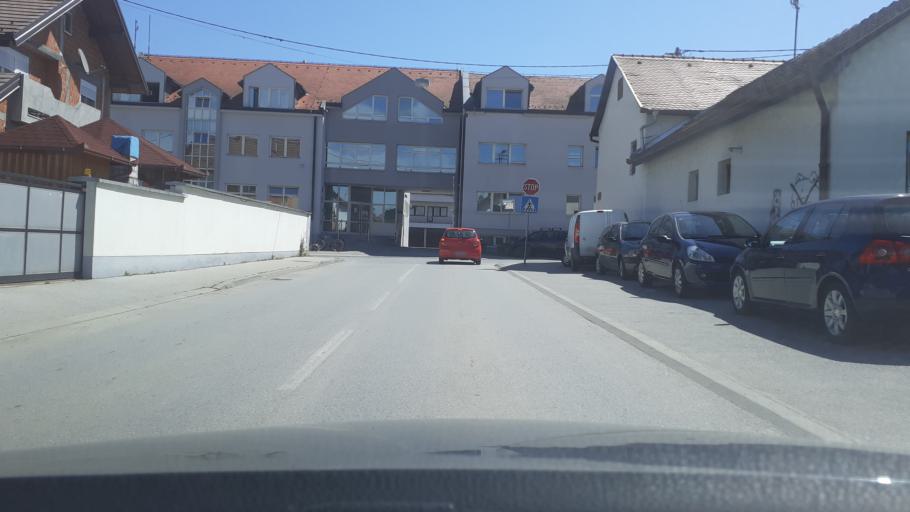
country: HR
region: Pozesko-Slavonska
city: Pozega
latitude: 45.3360
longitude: 17.6756
